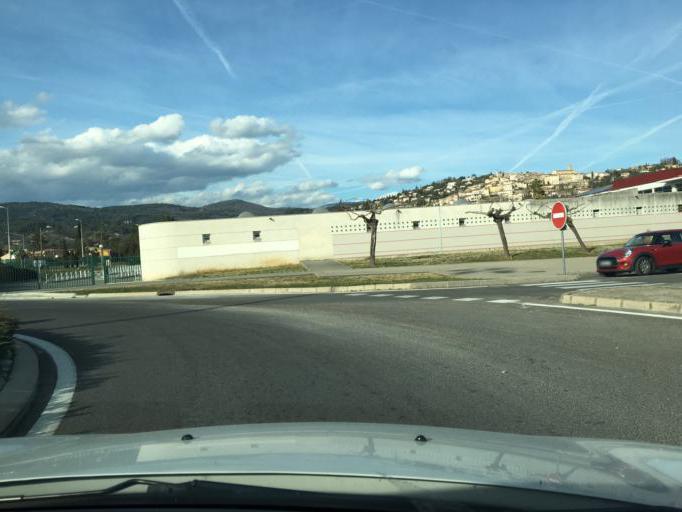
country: FR
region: Provence-Alpes-Cote d'Azur
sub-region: Departement du Var
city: Fayence
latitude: 43.6148
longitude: 6.6879
